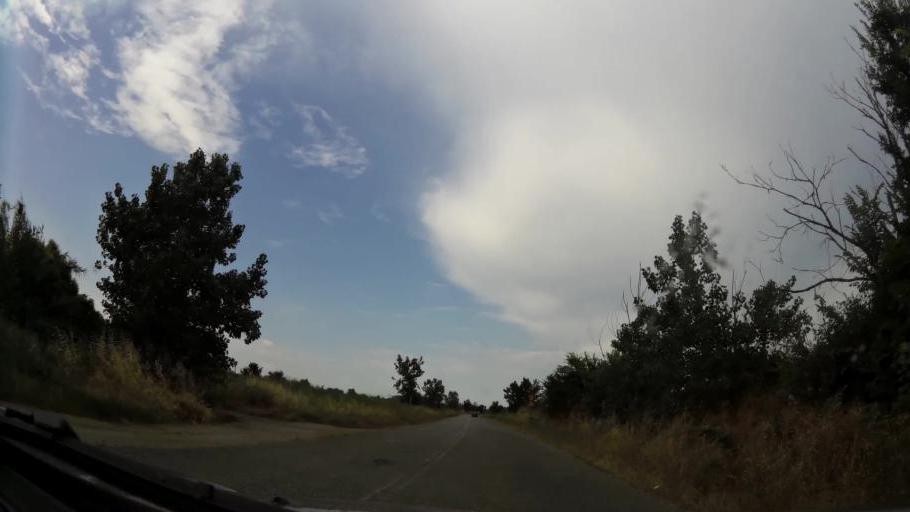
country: GR
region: Central Macedonia
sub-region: Nomos Pierias
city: Paralia
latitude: 40.2815
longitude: 22.6016
